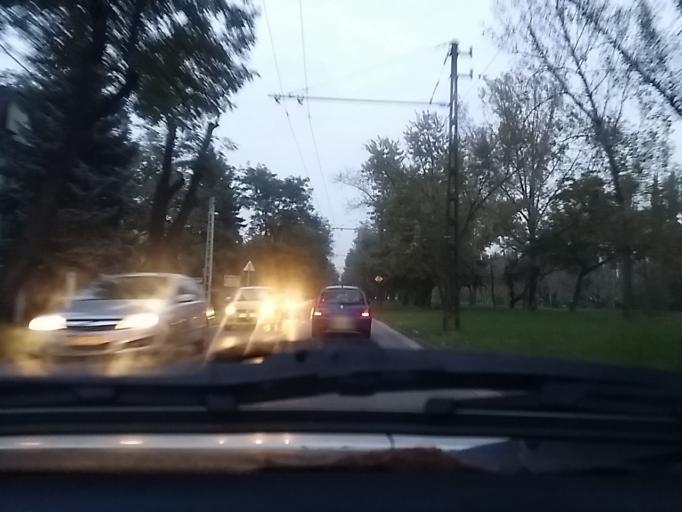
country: HU
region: Budapest
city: Budapest XIV. keruelet
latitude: 47.5223
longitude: 19.1312
